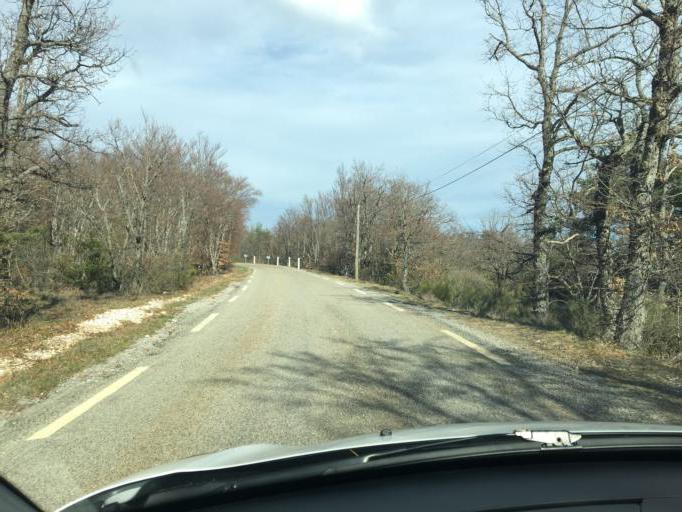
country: FR
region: Provence-Alpes-Cote d'Azur
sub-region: Departement du Vaucluse
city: Saint-Saturnin-les-Apt
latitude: 43.9739
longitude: 5.4650
